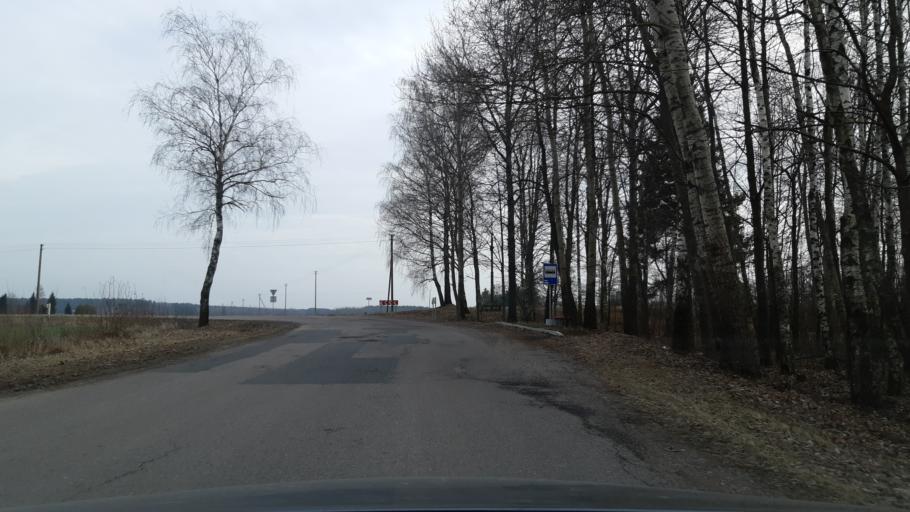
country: LT
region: Marijampoles apskritis
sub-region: Marijampole Municipality
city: Marijampole
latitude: 54.7172
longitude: 23.3306
